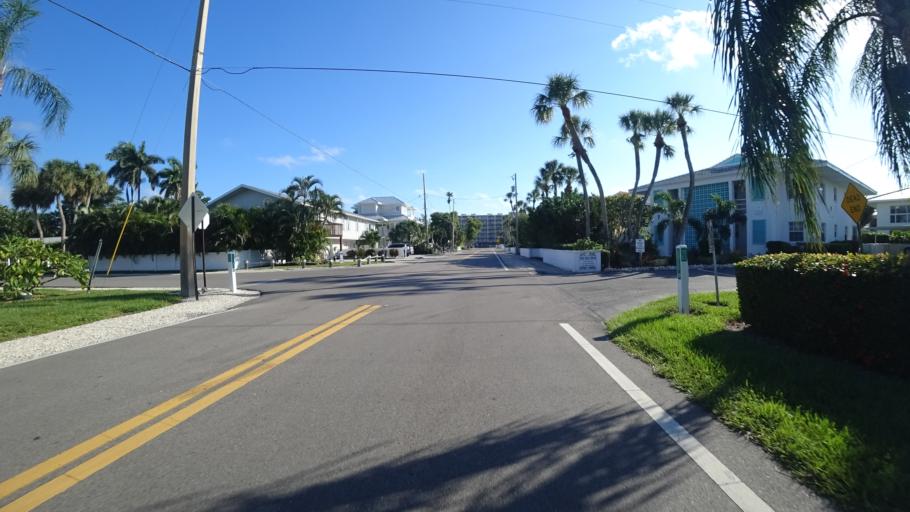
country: US
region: Florida
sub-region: Manatee County
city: Holmes Beach
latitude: 27.5075
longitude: -82.7174
